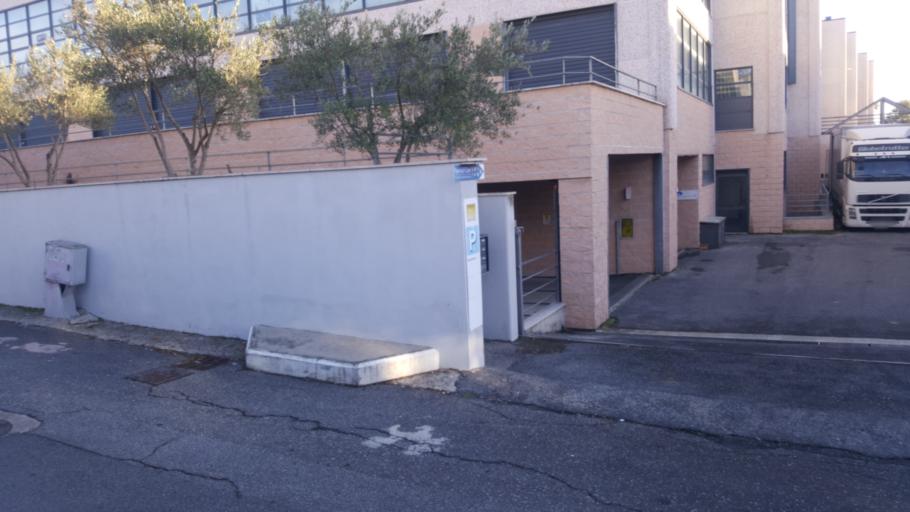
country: IT
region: Latium
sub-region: Citta metropolitana di Roma Capitale
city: Formello
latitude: 42.0502
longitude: 12.4032
